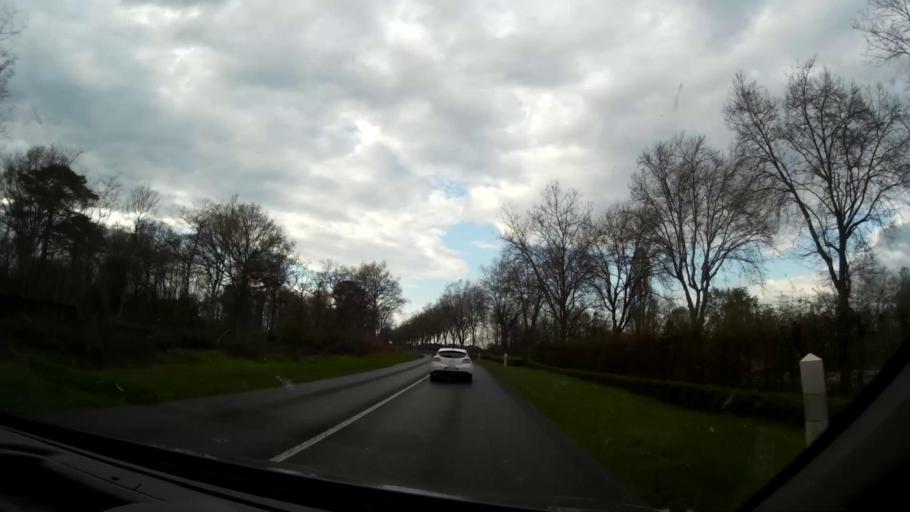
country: FR
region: Centre
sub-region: Departement du Loir-et-Cher
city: Cormeray
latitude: 47.4706
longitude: 1.4238
